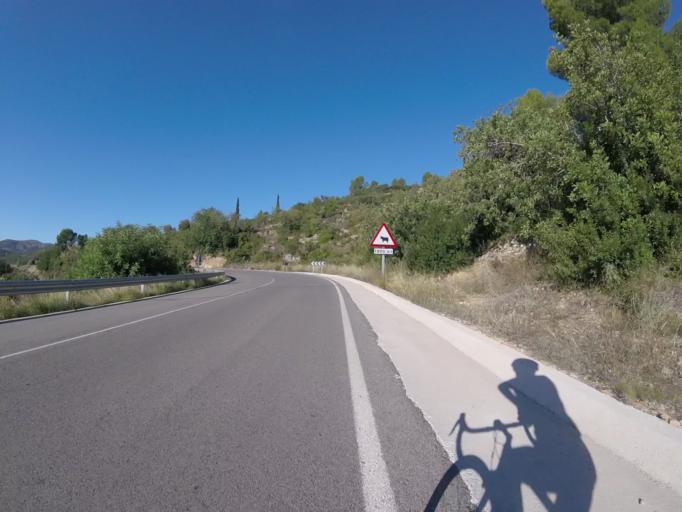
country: ES
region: Valencia
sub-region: Provincia de Castello
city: Cervera del Maestre
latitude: 40.4572
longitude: 0.2712
